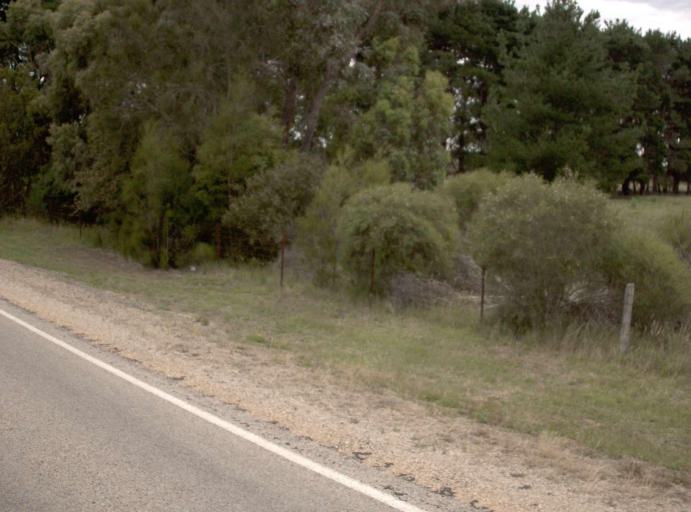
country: AU
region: Victoria
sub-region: East Gippsland
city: Bairnsdale
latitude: -37.8677
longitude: 147.5618
